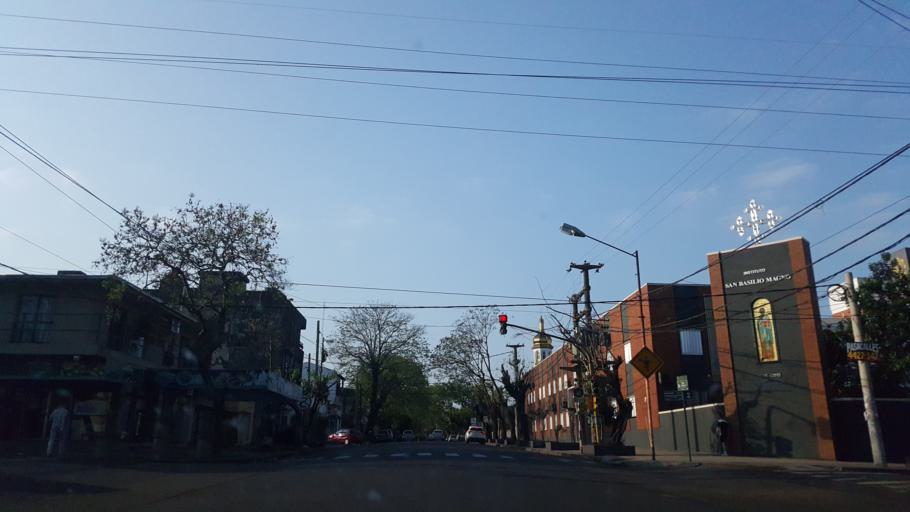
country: AR
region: Misiones
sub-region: Departamento de Capital
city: Posadas
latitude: -27.3782
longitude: -55.8953
